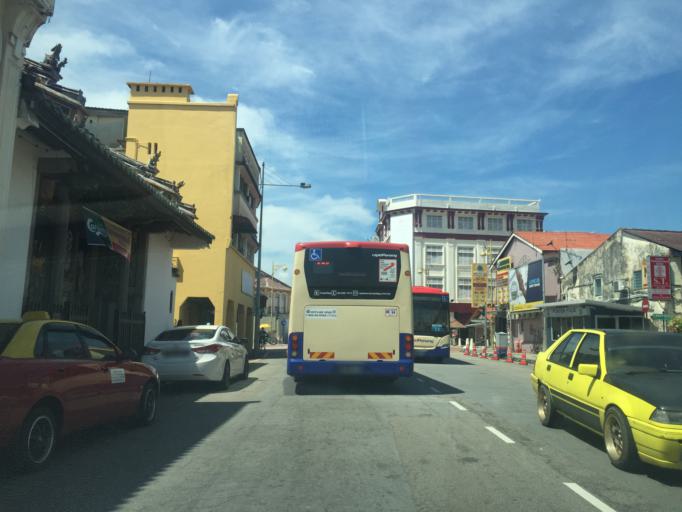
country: MY
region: Penang
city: George Town
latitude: 5.4167
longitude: 100.3383
